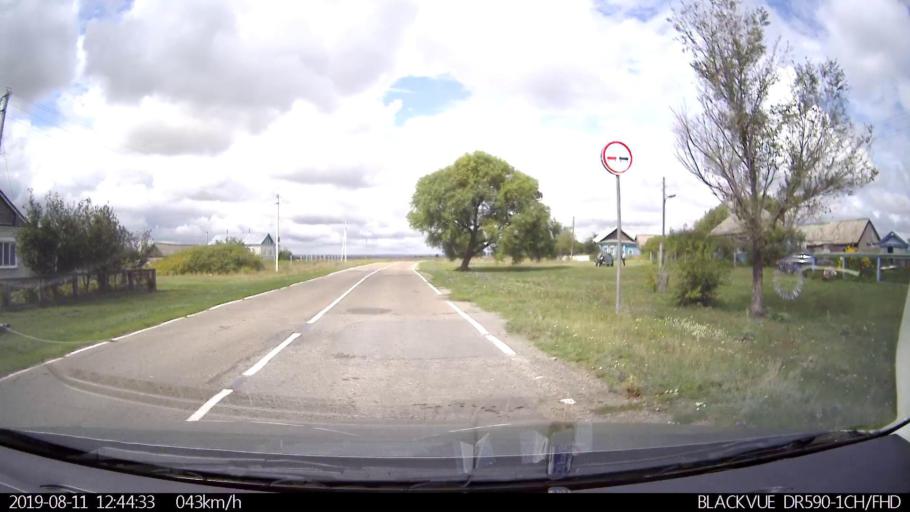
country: RU
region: Ulyanovsk
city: Ignatovka
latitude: 53.8553
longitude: 47.7352
